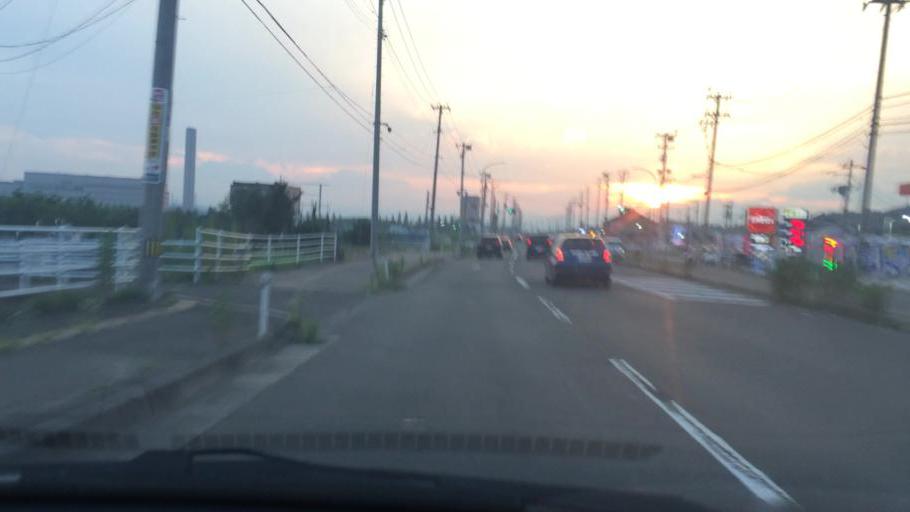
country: JP
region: Miyagi
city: Rifu
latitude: 38.3095
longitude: 140.9304
